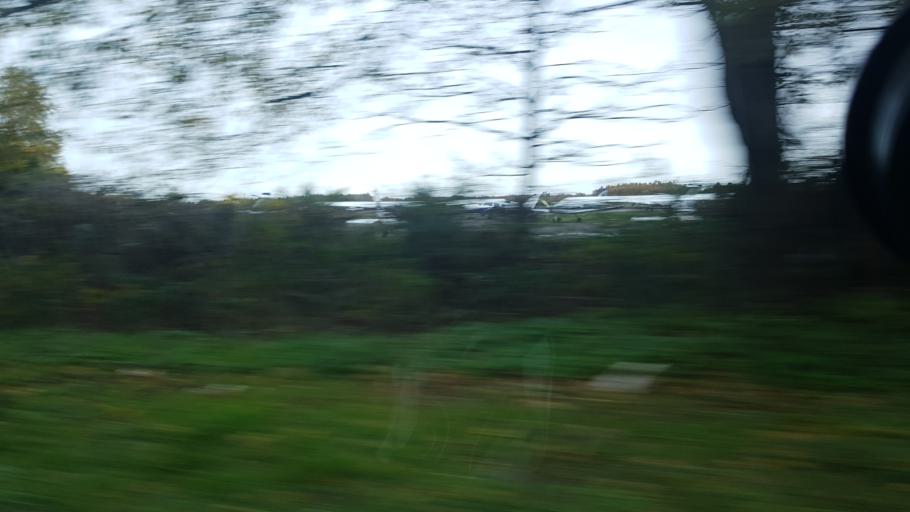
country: GB
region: England
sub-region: Hampshire
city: Yateley
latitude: 51.3221
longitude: -0.8419
